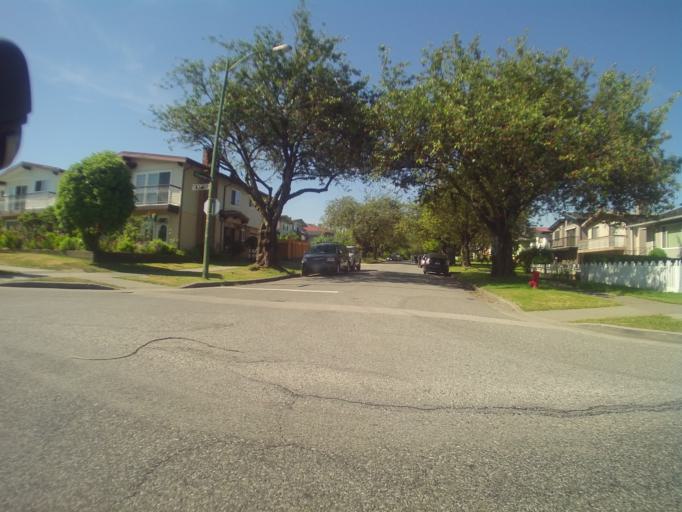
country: CA
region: British Columbia
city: Vancouver
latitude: 49.2182
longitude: -123.0800
